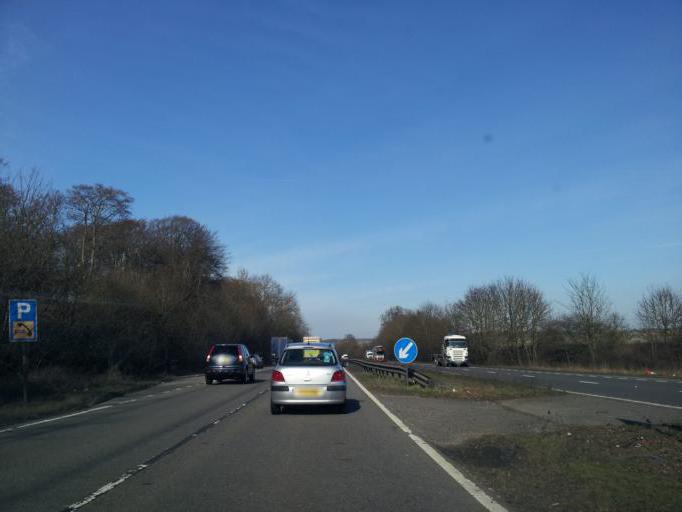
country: GB
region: England
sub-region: Lincolnshire
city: Grantham
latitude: 52.8469
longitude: -0.6279
